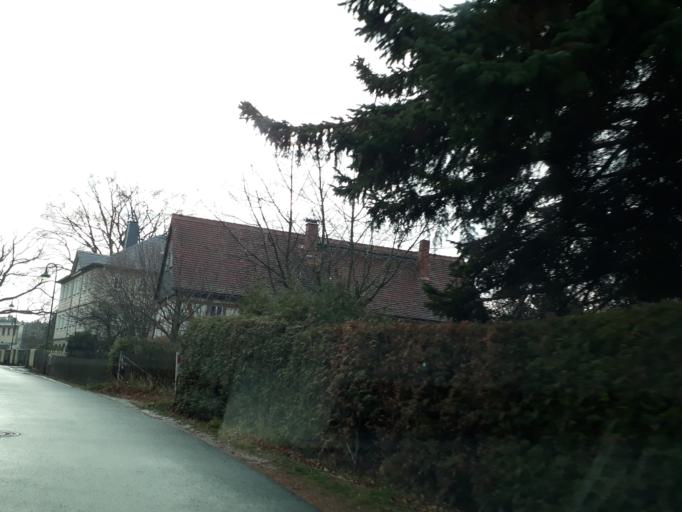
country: DE
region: Saxony
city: Niedercunnersdorf
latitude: 51.0559
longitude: 14.6570
